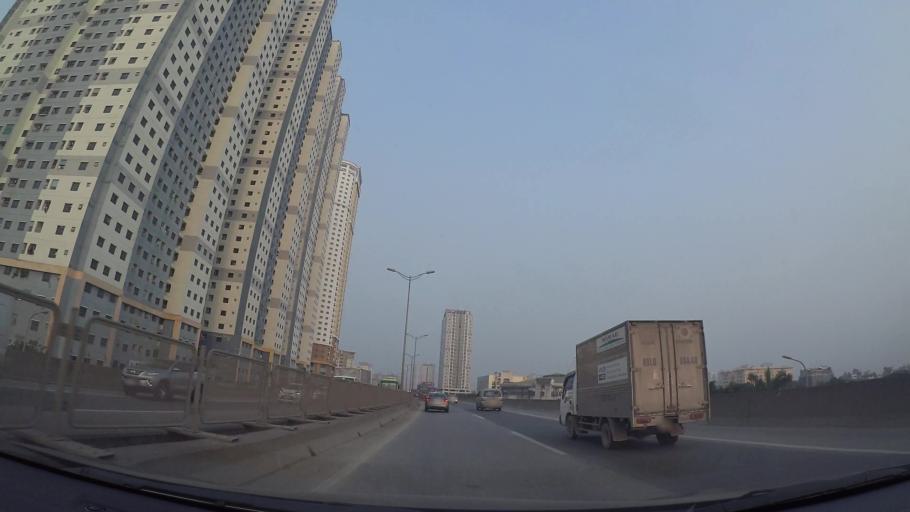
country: VN
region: Ha Noi
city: Thanh Xuan
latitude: 20.9727
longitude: 105.8188
